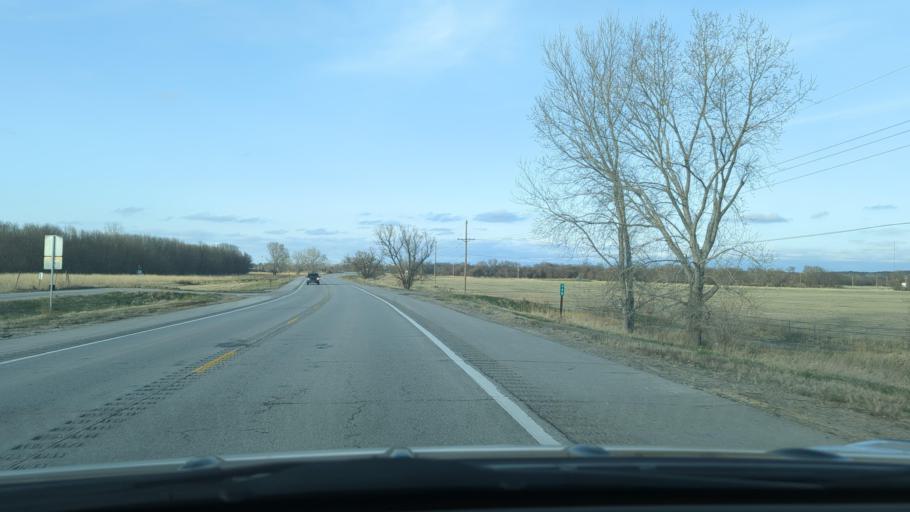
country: US
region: Nebraska
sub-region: Saunders County
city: Ashland
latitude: 41.0525
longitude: -96.3376
